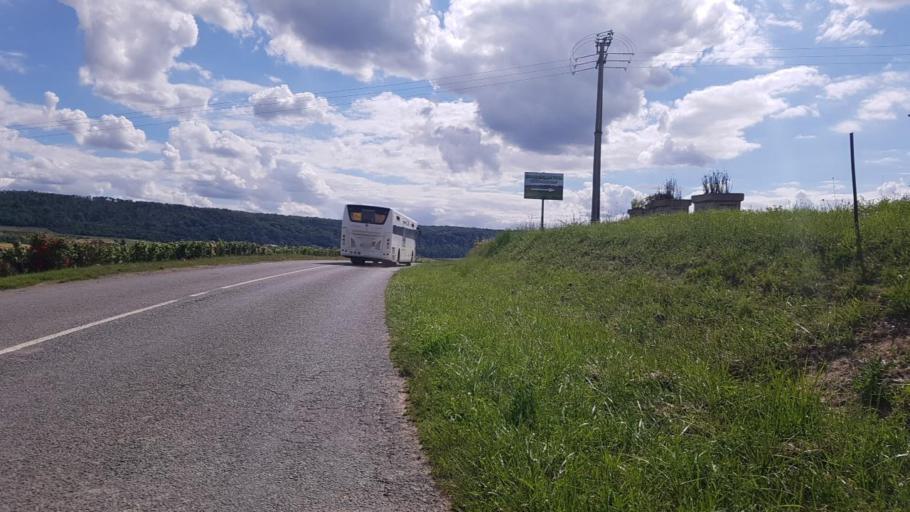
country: FR
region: Champagne-Ardenne
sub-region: Departement de la Marne
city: Dormans
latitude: 49.0644
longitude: 3.5901
